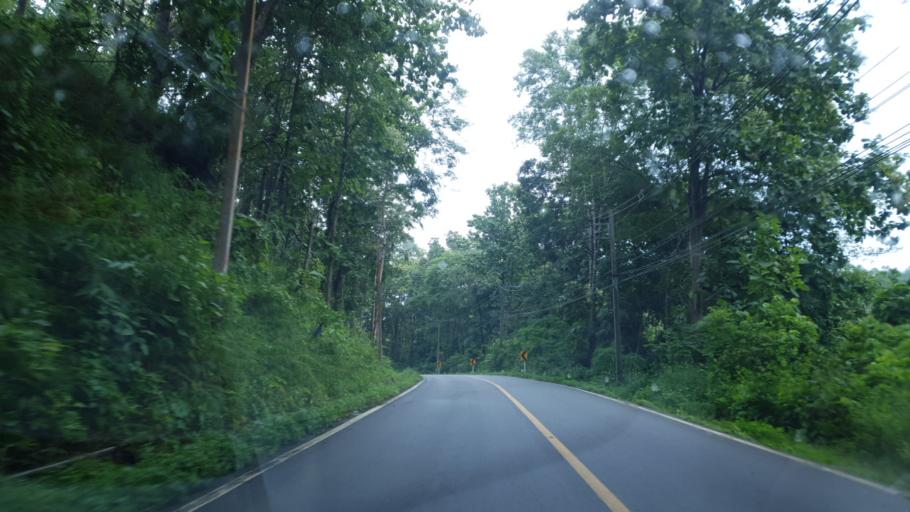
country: TH
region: Mae Hong Son
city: Ban Huai I Huak
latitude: 18.1381
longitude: 97.9835
